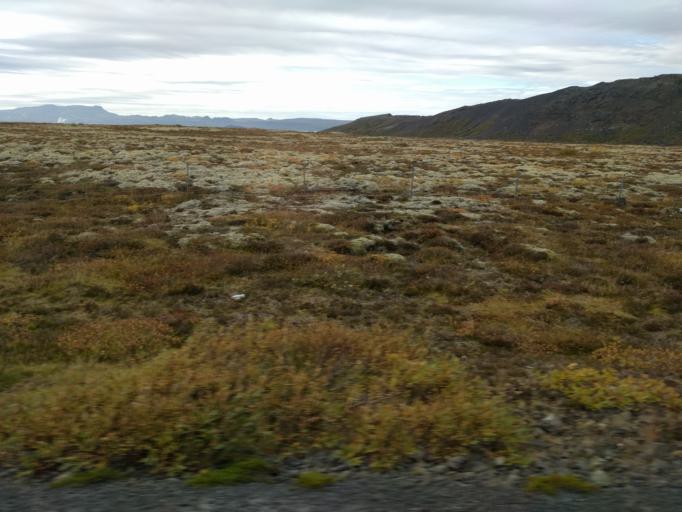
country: IS
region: South
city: Hveragerdi
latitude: 64.2164
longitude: -21.0508
